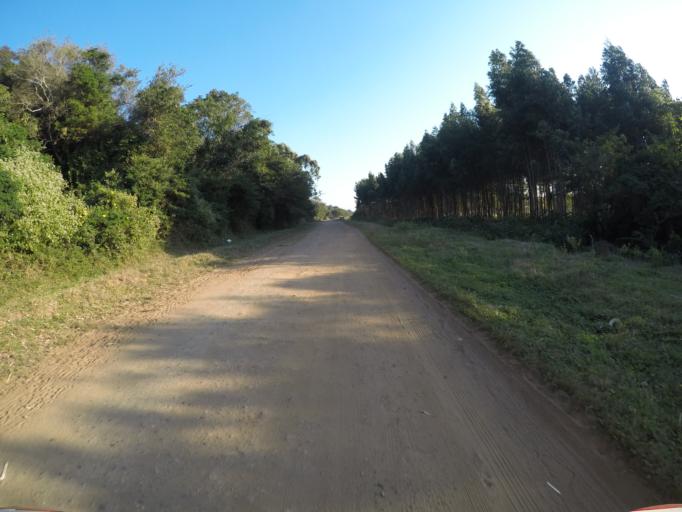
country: ZA
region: KwaZulu-Natal
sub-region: uThungulu District Municipality
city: KwaMbonambi
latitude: -28.7021
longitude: 32.1906
